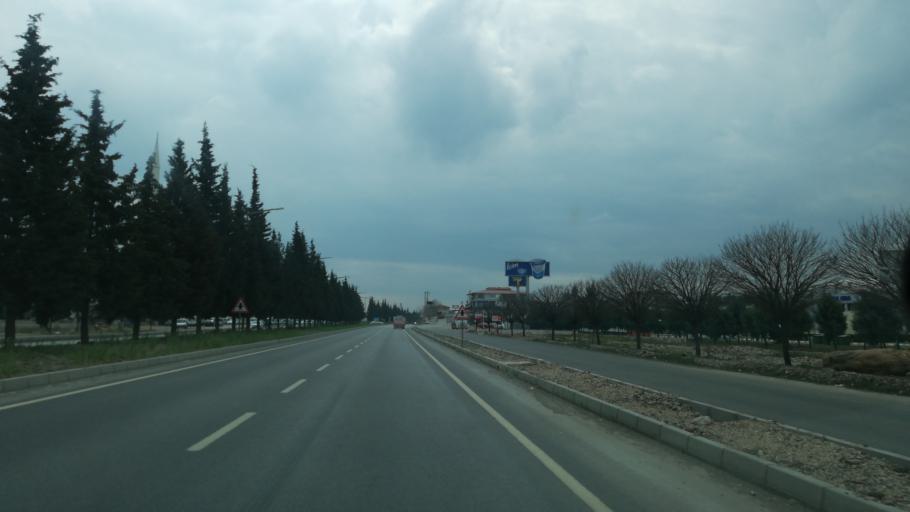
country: TR
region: Kahramanmaras
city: Turkoglu
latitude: 37.4196
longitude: 36.8819
